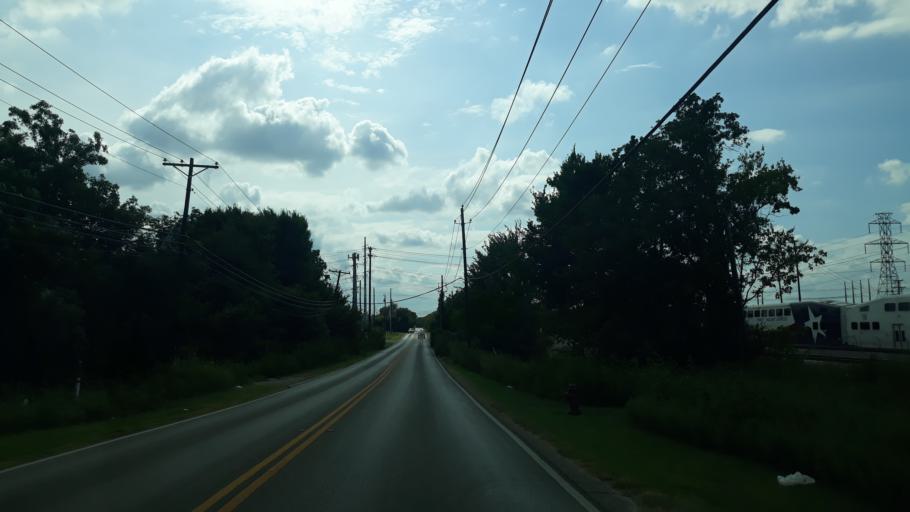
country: US
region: Texas
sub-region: Tarrant County
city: Euless
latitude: 32.8162
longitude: -97.0211
